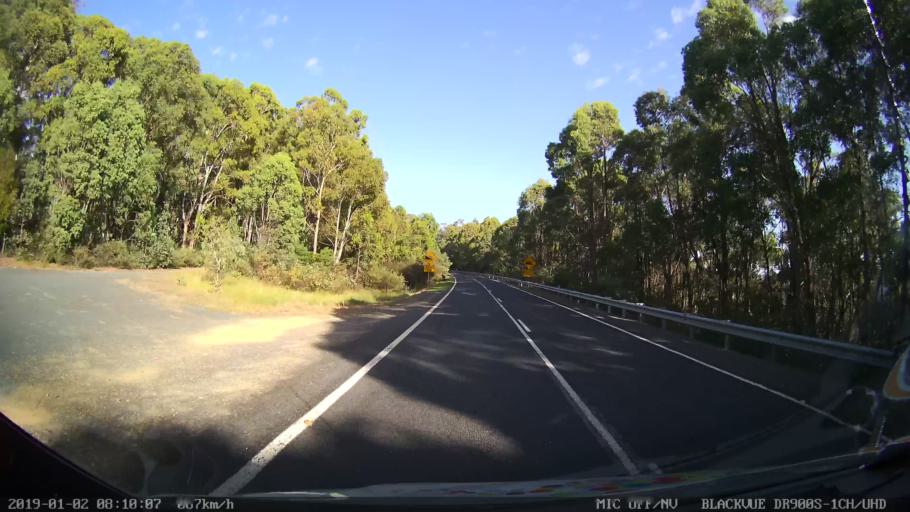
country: AU
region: New South Wales
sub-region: Tumut Shire
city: Tumut
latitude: -35.6012
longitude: 148.3736
